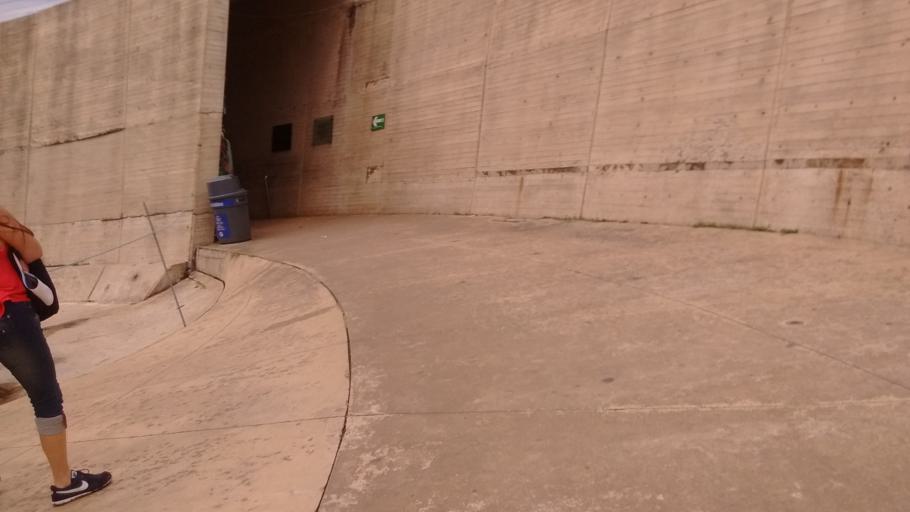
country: CO
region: Antioquia
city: Medellin
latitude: 6.2696
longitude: -75.5649
